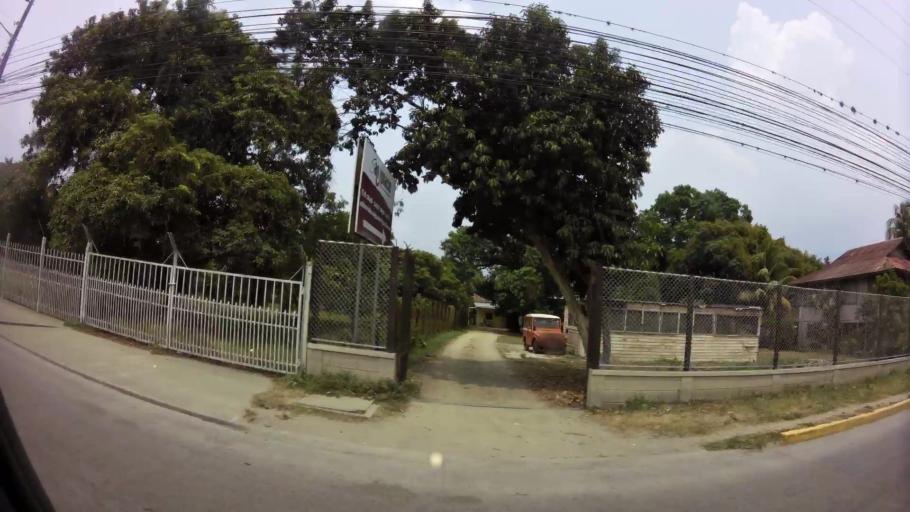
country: HN
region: Yoro
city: El Progreso
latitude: 15.3966
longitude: -87.8123
